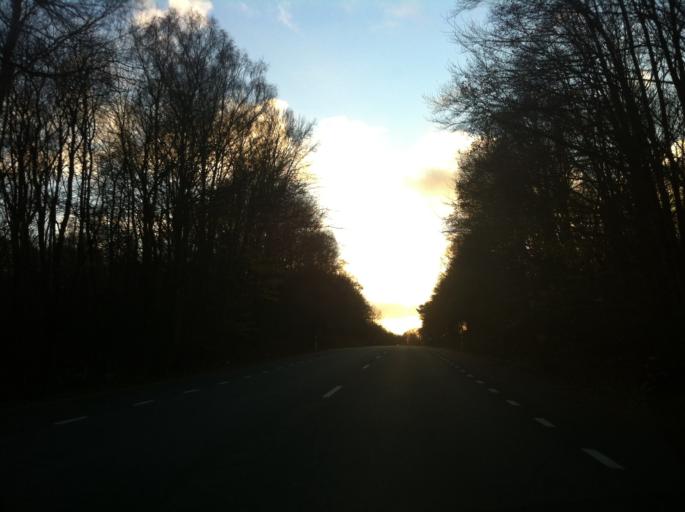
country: SE
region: Skane
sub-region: Hassleholms Kommun
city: Sosdala
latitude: 56.0285
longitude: 13.6783
